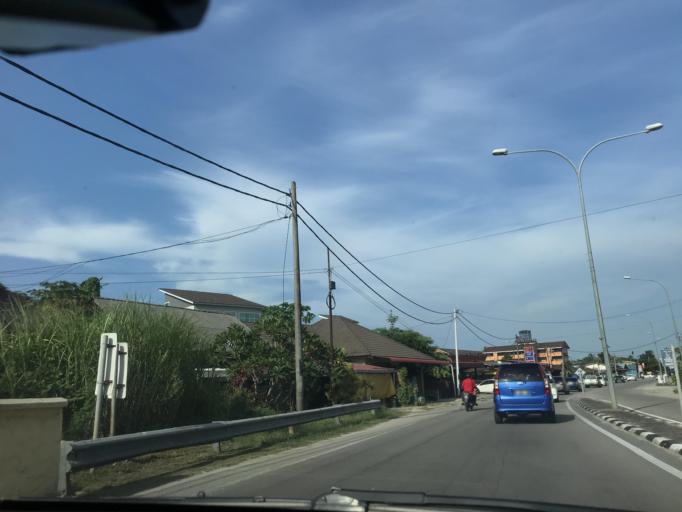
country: MY
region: Kelantan
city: Kota Bharu
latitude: 6.1242
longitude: 102.2763
